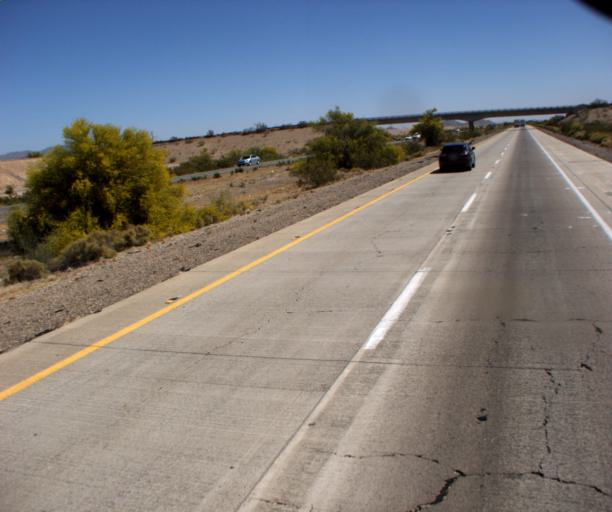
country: US
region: Arizona
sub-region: Maricopa County
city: Buckeye
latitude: 33.4474
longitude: -112.7146
